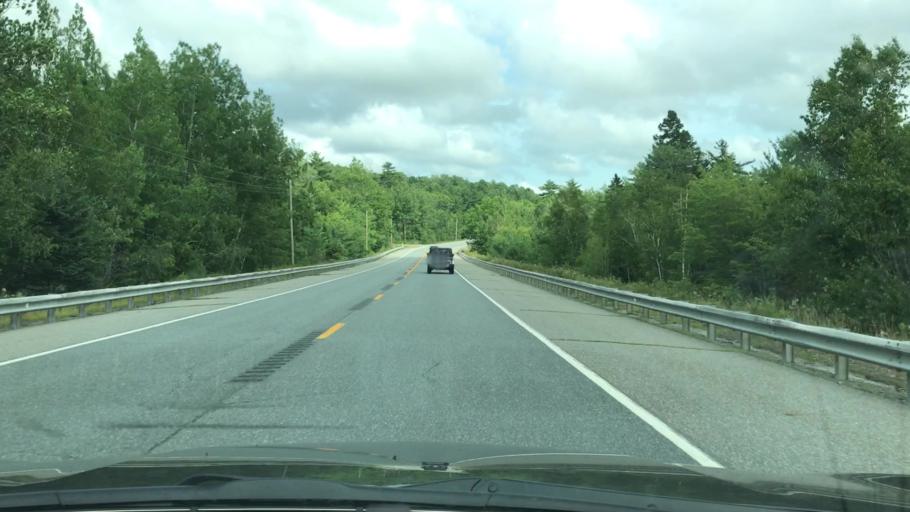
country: US
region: Maine
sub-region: Hancock County
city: Surry
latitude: 44.5638
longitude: -68.5939
